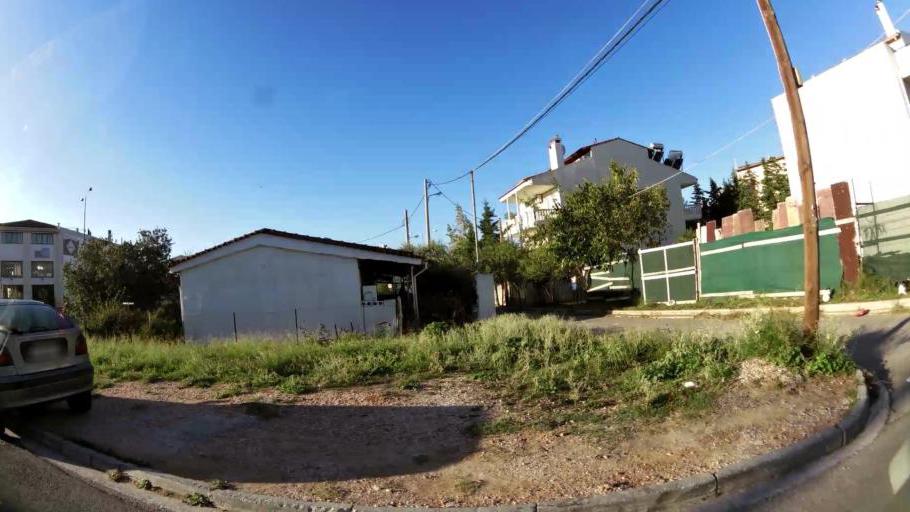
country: GR
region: Attica
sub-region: Nomarchia Athinas
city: Agia Paraskevi
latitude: 38.0257
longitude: 23.8409
